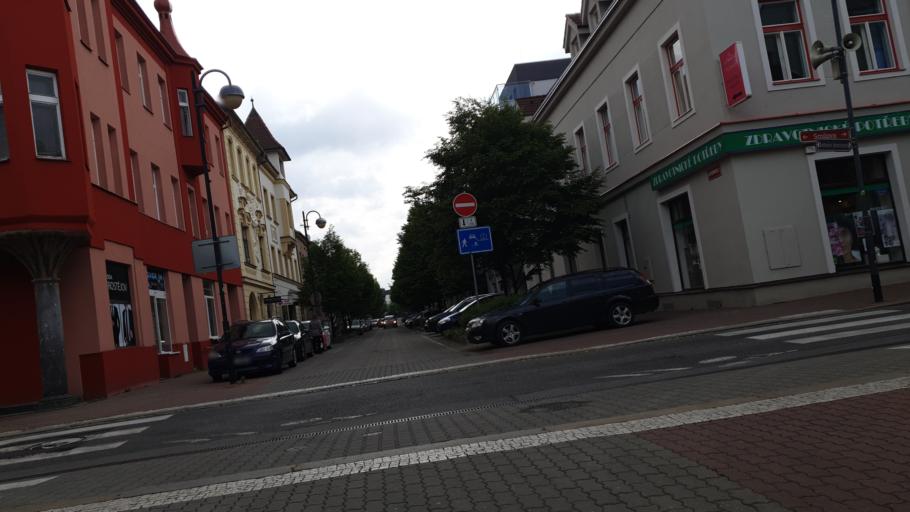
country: CZ
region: Pardubicky
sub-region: Okres Pardubice
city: Pardubice
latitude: 50.0344
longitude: 15.7720
